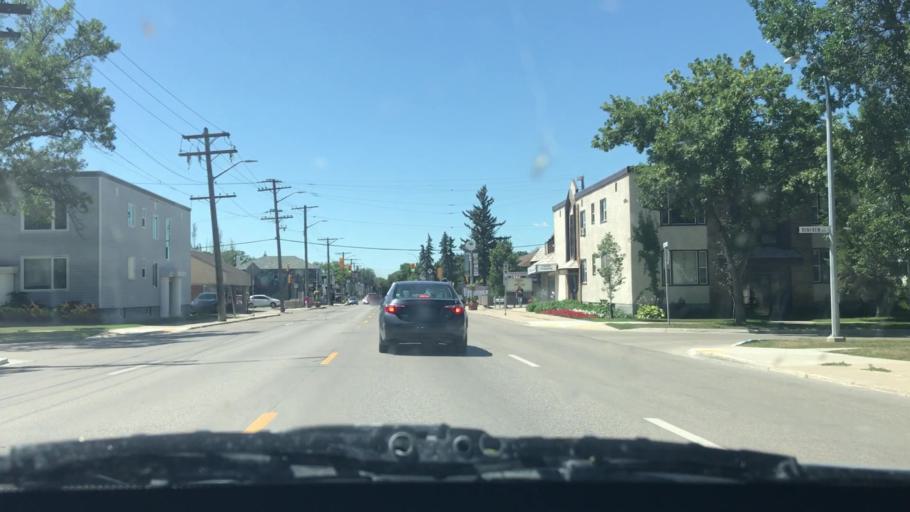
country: CA
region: Manitoba
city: Winnipeg
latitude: 49.8742
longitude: -97.1953
